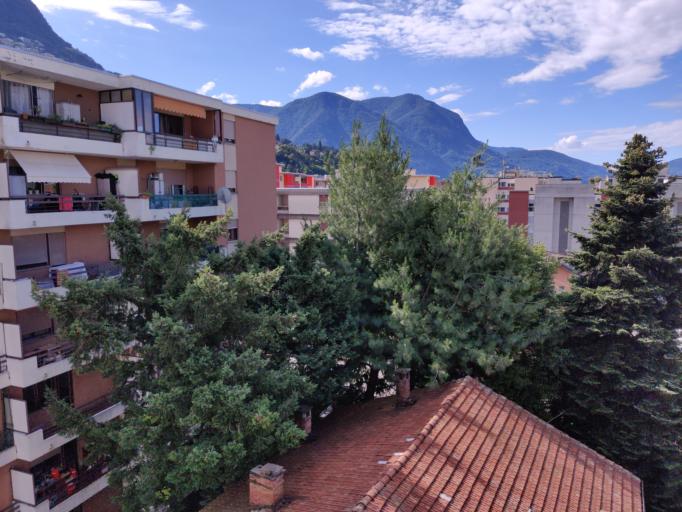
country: CH
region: Ticino
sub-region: Lugano District
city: Viganello
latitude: 46.0149
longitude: 8.9641
